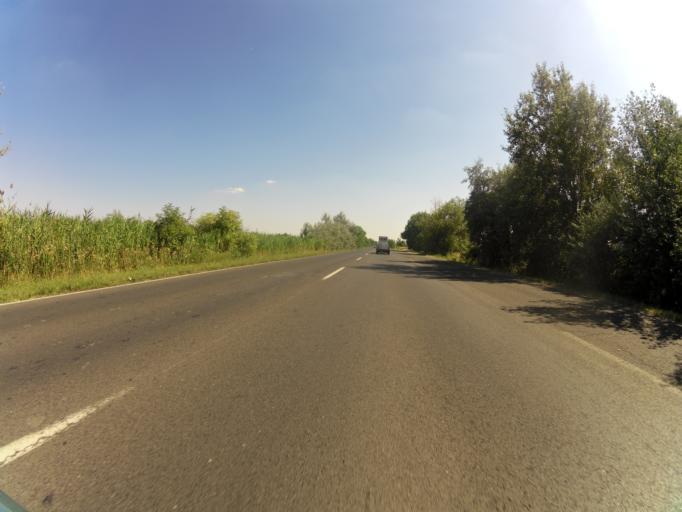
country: HU
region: Csongrad
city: Szatymaz
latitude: 46.3195
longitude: 20.0634
